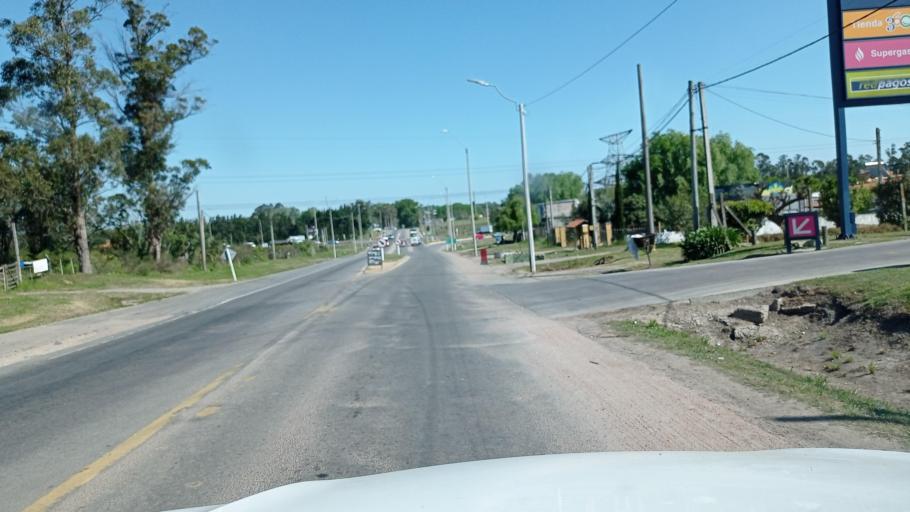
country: UY
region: Canelones
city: La Paz
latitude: -34.7929
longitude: -56.1656
